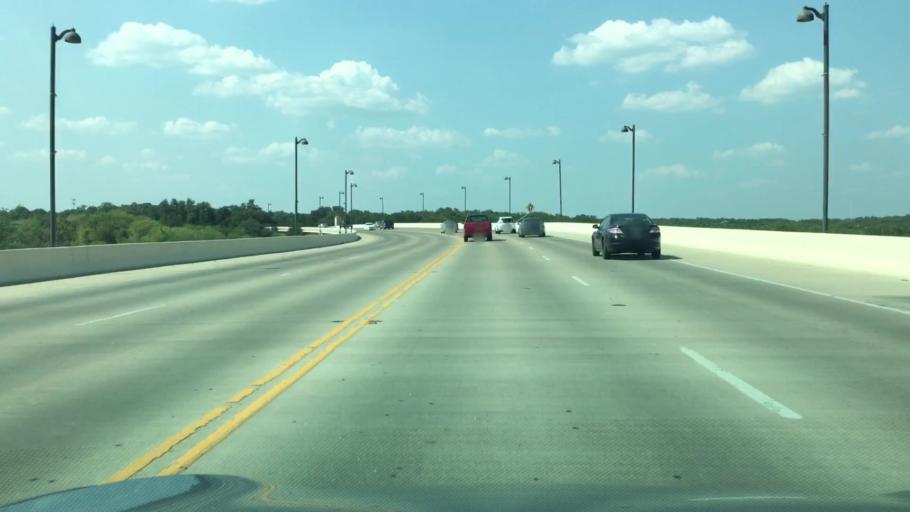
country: US
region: Texas
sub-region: Hays County
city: San Marcos
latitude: 29.8718
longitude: -97.9660
